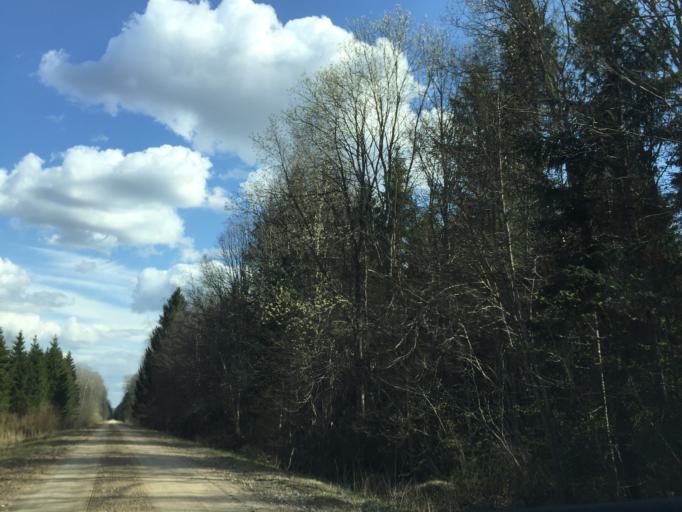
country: LV
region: Skriveri
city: Skriveri
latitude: 56.8017
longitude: 25.1944
